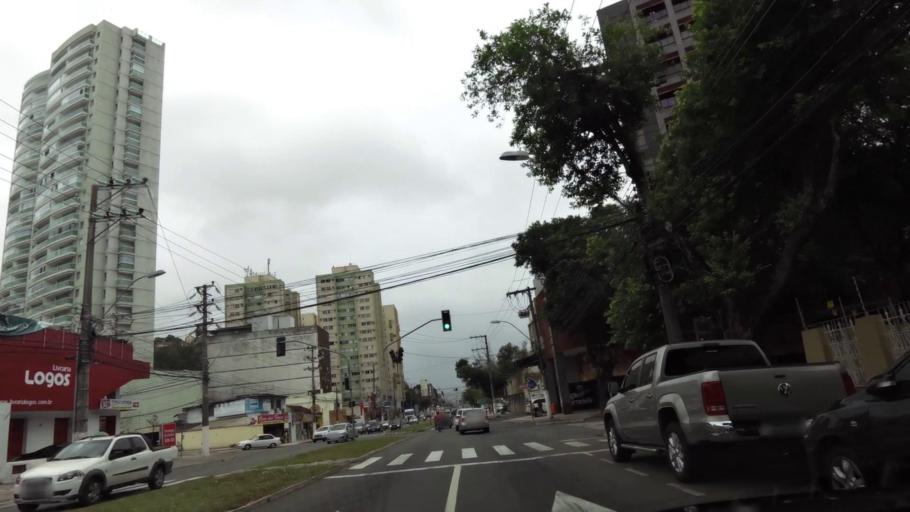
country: BR
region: Espirito Santo
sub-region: Vila Velha
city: Vila Velha
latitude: -20.3128
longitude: -40.3021
